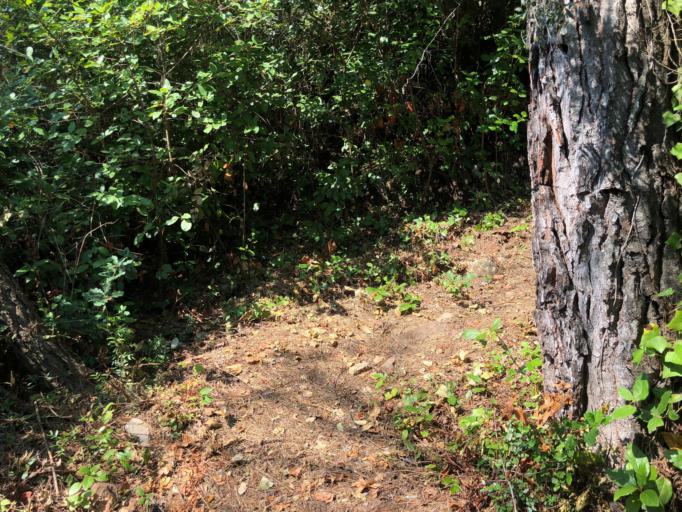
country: ES
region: Catalonia
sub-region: Provincia de Barcelona
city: Corbera de Llobregat
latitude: 41.4218
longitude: 1.9075
